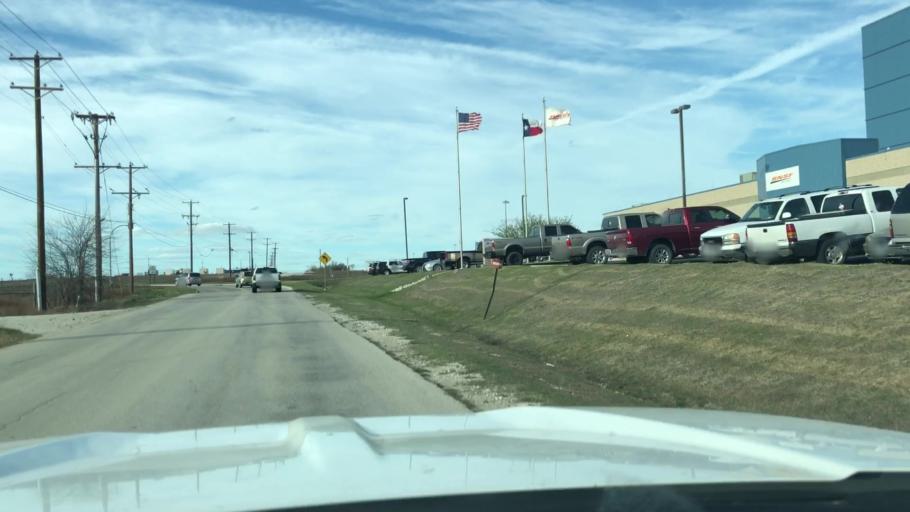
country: US
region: Texas
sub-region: Tarrant County
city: Haslet
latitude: 32.9912
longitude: -97.3561
